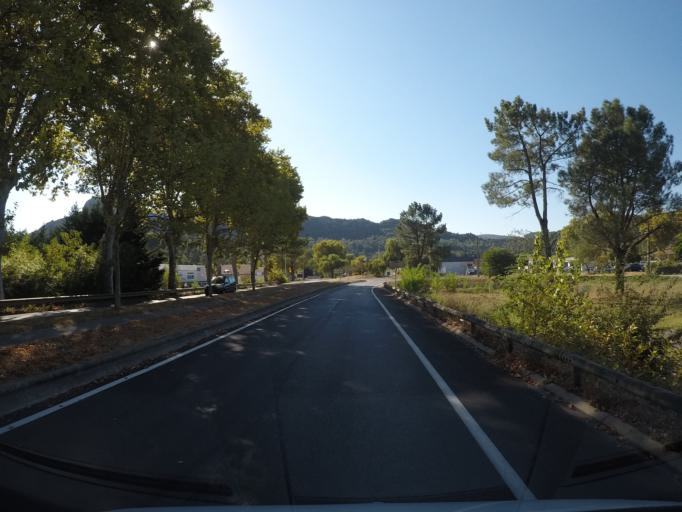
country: FR
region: Languedoc-Roussillon
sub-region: Departement du Gard
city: Anduze
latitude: 44.0629
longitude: 3.9723
